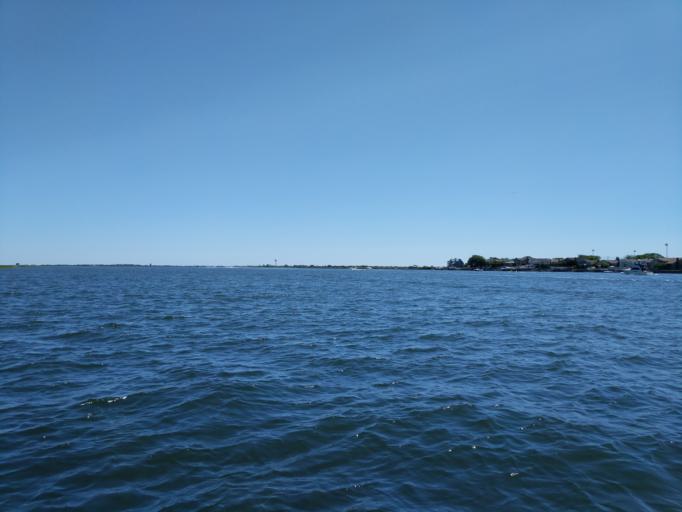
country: US
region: New York
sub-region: Nassau County
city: Barnum Island
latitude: 40.5975
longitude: -73.6345
